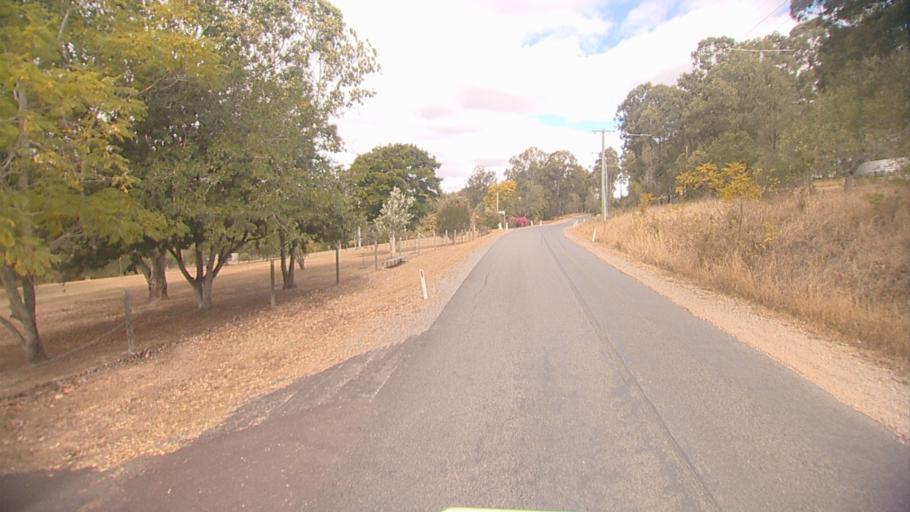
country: AU
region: Queensland
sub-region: Logan
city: Cedar Vale
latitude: -27.8816
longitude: 153.0279
